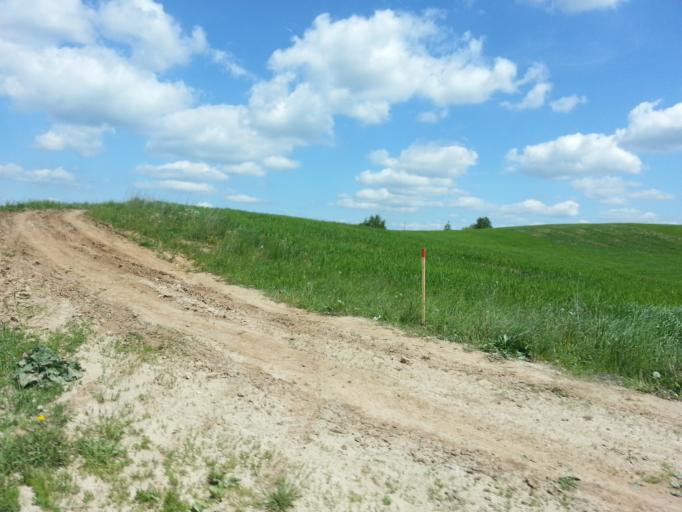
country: LT
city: Lentvaris
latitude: 54.6794
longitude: 24.9864
